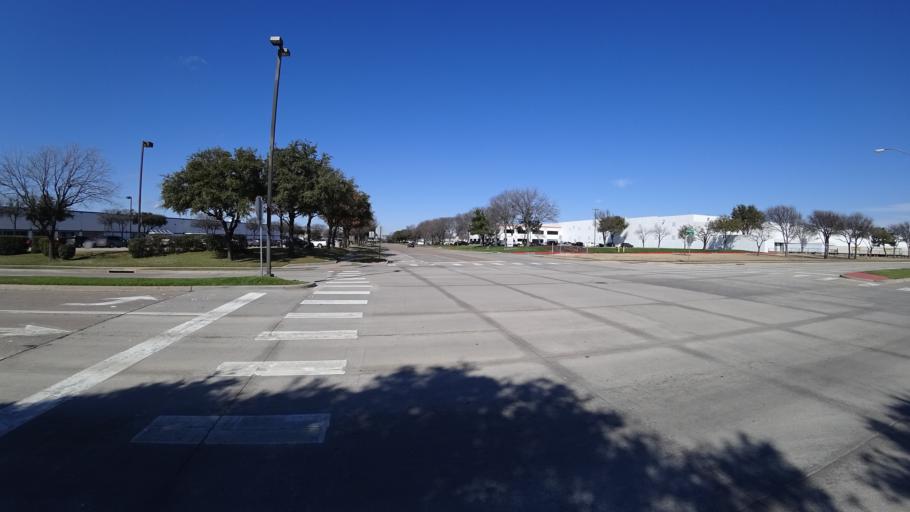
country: US
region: Texas
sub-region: Denton County
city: Lewisville
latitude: 33.0215
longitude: -96.9733
